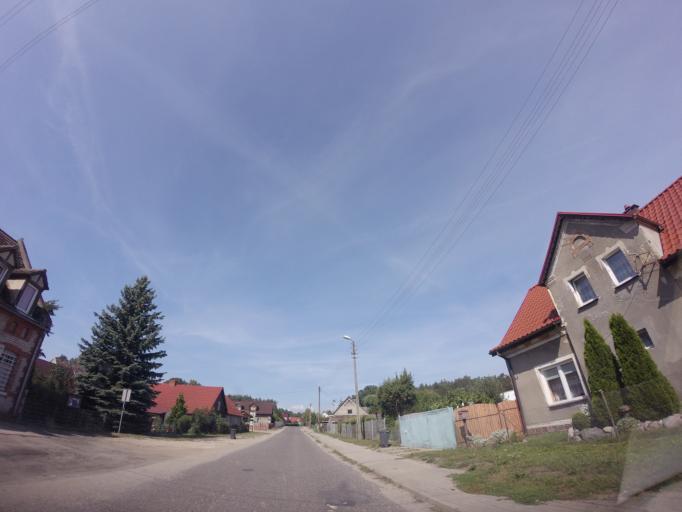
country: PL
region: Lubusz
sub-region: Powiat strzelecko-drezdenecki
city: Drezdenko
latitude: 52.7188
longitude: 15.7895
